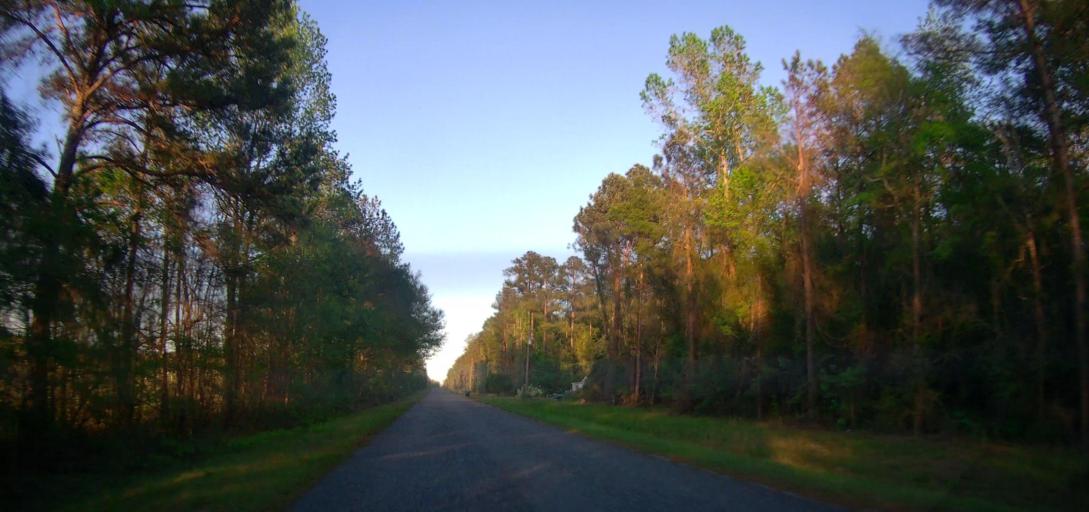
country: US
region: Georgia
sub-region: Talbot County
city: Talbotton
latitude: 32.5352
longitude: -84.5949
